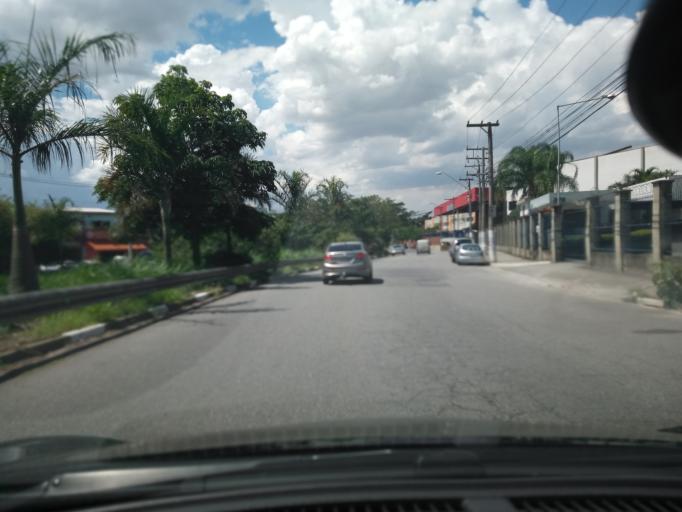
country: BR
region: Sao Paulo
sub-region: Sao Bernardo Do Campo
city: Sao Bernardo do Campo
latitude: -23.6943
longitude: -46.5800
